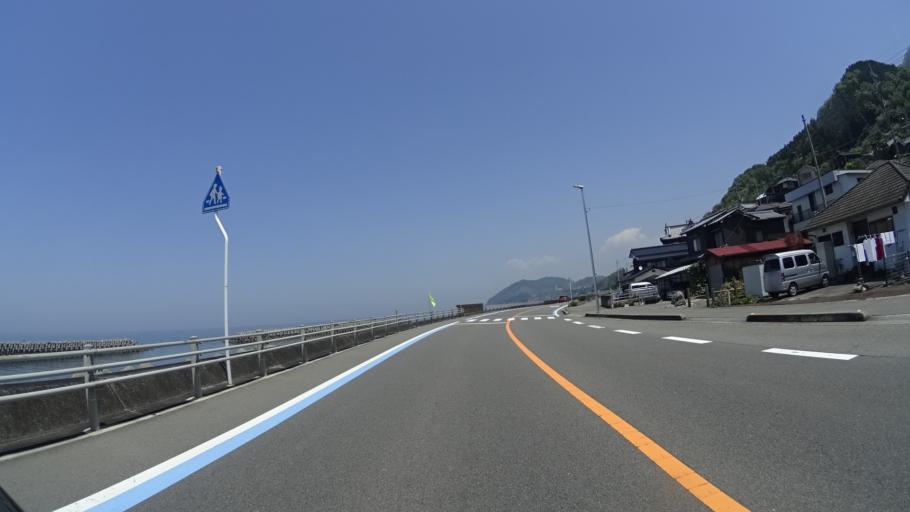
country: JP
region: Ehime
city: Iyo
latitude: 33.6944
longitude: 132.6491
